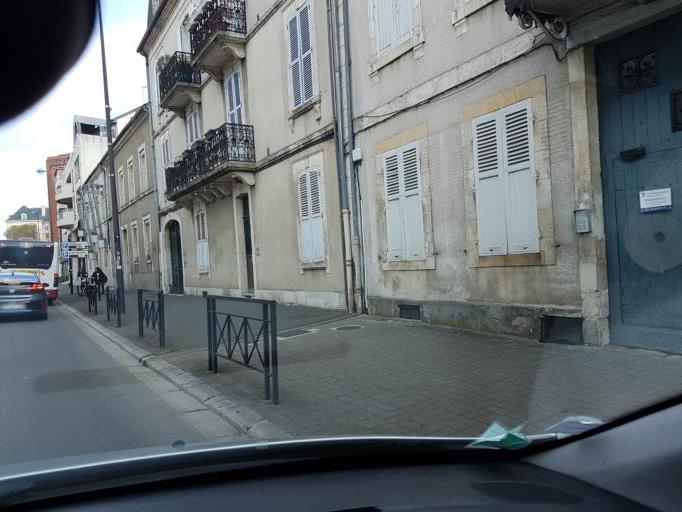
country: FR
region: Centre
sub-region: Departement du Cher
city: Bourges
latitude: 47.0782
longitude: 2.3995
